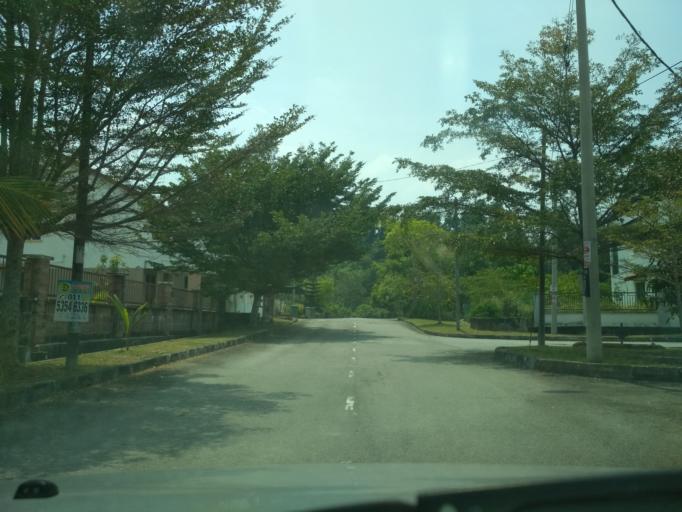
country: MY
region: Kedah
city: Kulim
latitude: 5.3605
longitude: 100.5366
